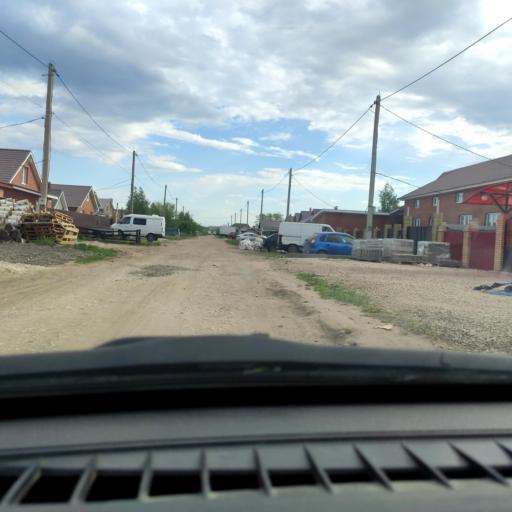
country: RU
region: Samara
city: Tol'yatti
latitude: 53.5711
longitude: 49.4110
